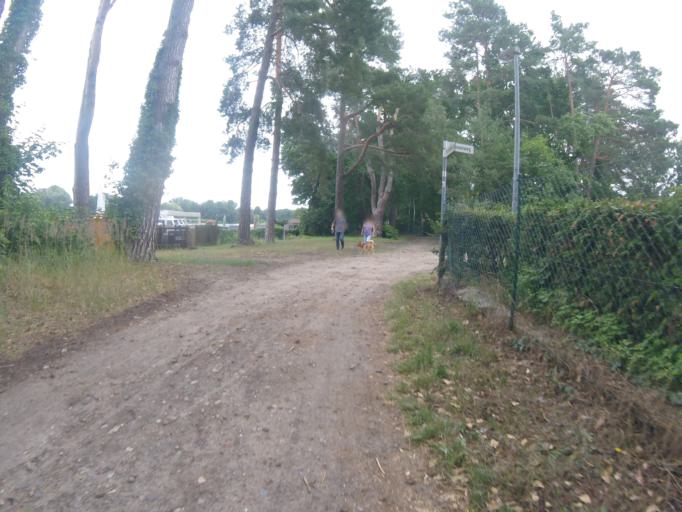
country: DE
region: Brandenburg
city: Bestensee
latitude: 52.2902
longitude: 13.7122
